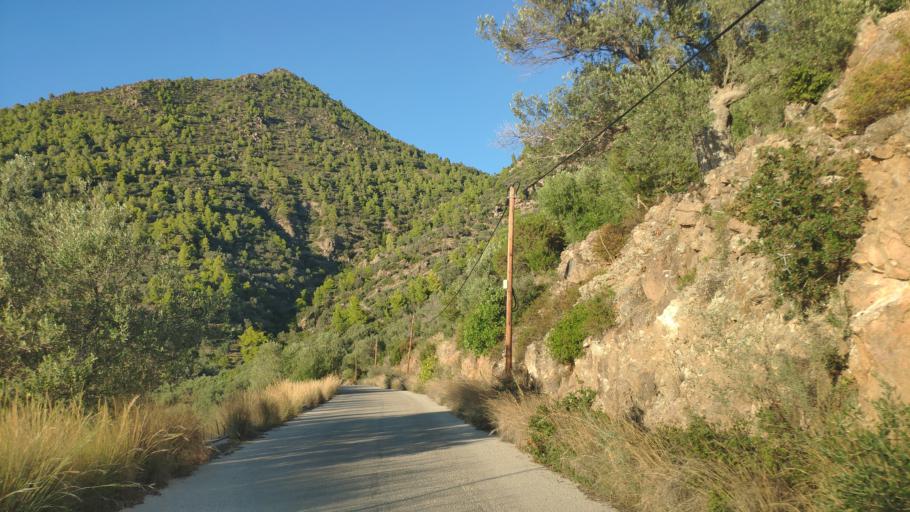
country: GR
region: Attica
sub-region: Nomos Piraios
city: Megalochori
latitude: 37.5977
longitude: 23.3366
